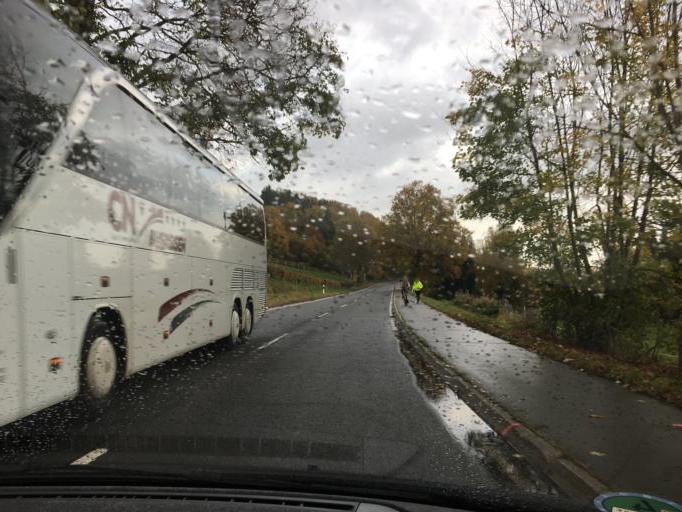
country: DE
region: North Rhine-Westphalia
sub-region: Regierungsbezirk Koln
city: Simmerath
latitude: 50.6219
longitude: 6.3751
